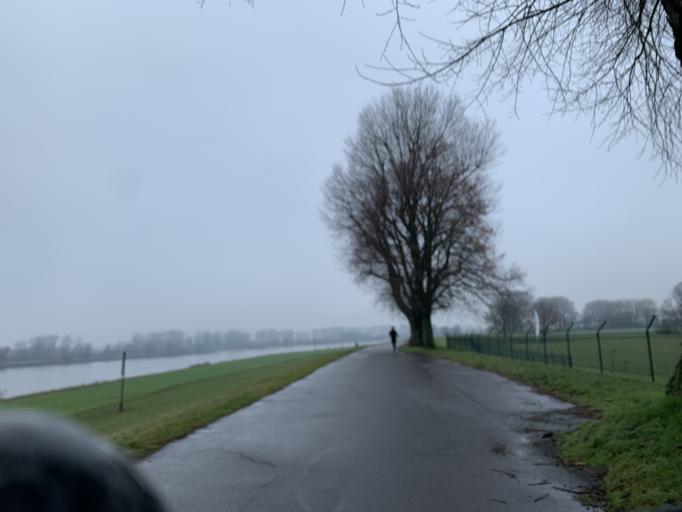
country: DE
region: North Rhine-Westphalia
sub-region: Regierungsbezirk Dusseldorf
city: Meerbusch
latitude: 51.2631
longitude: 6.7159
